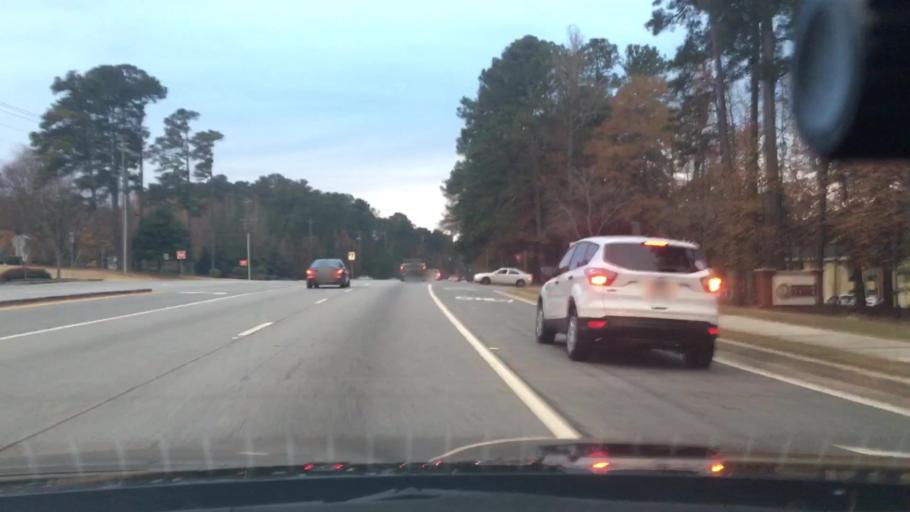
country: US
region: Georgia
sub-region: Fayette County
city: Peachtree City
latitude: 33.3998
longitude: -84.5950
